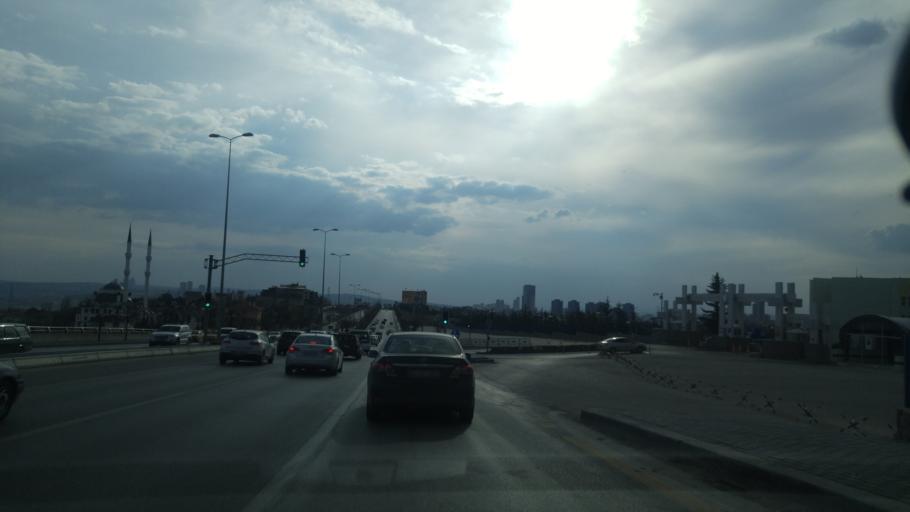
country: TR
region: Ankara
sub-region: Goelbasi
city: Golbasi
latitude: 39.8364
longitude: 32.7618
